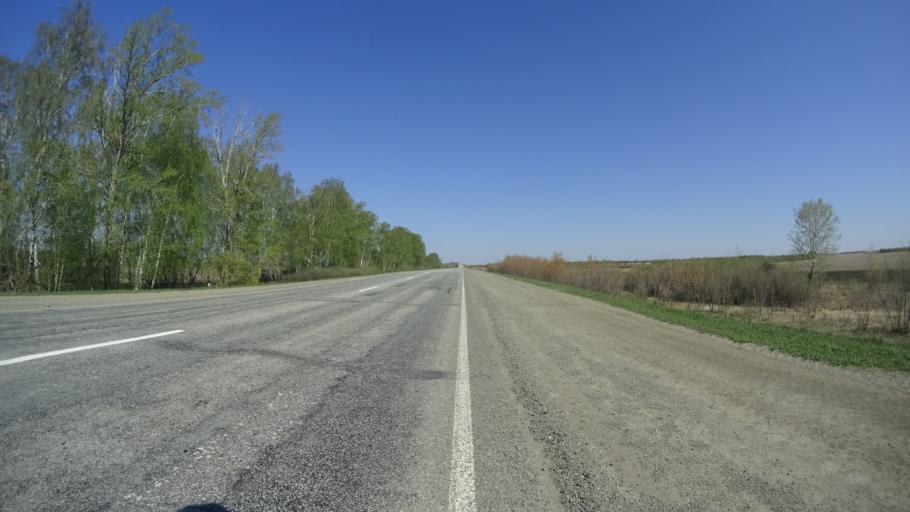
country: RU
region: Chelyabinsk
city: Troitsk
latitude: 54.1975
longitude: 61.4326
